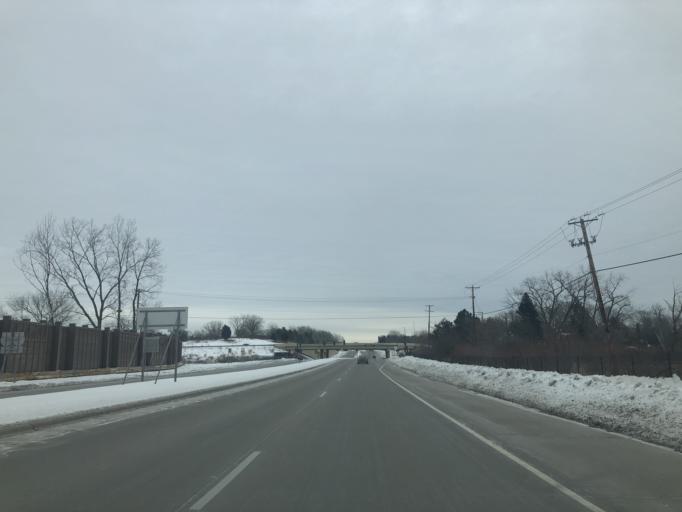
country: US
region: Minnesota
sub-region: Ramsey County
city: New Brighton
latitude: 45.0792
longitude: -93.1802
